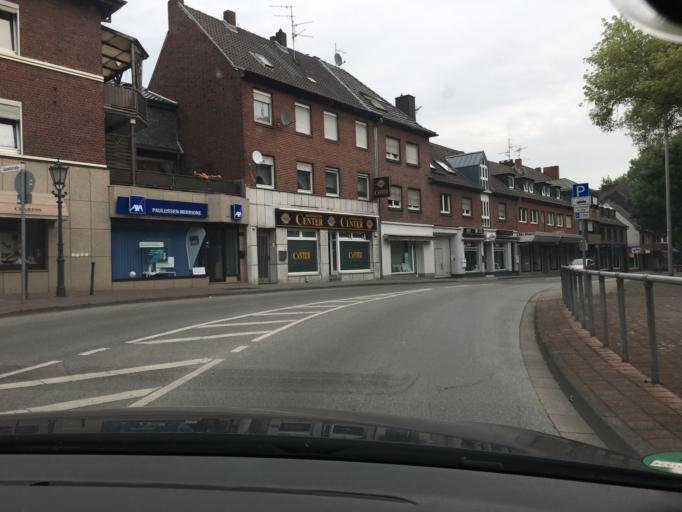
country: DE
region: North Rhine-Westphalia
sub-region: Regierungsbezirk Dusseldorf
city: Monchengladbach
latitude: 51.1298
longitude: 6.4132
